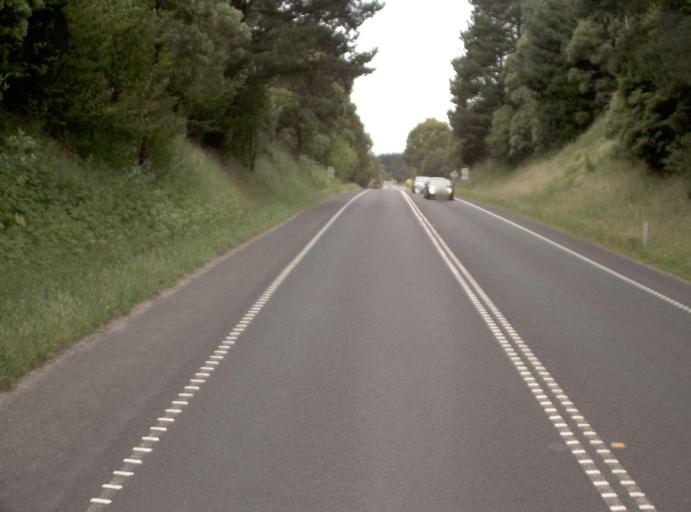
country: AU
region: Victoria
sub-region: Bass Coast
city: North Wonthaggi
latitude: -38.4490
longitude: 145.8335
